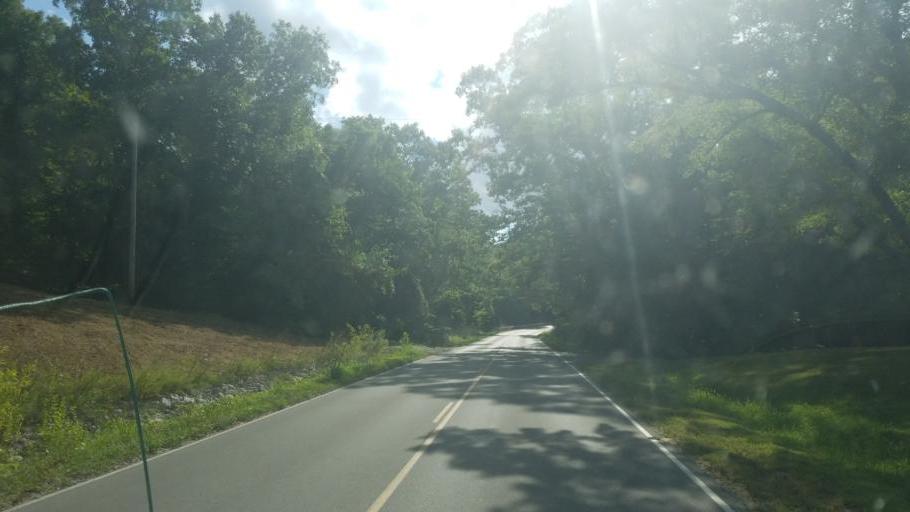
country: US
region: Illinois
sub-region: Union County
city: Cobden
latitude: 37.5444
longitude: -89.2700
